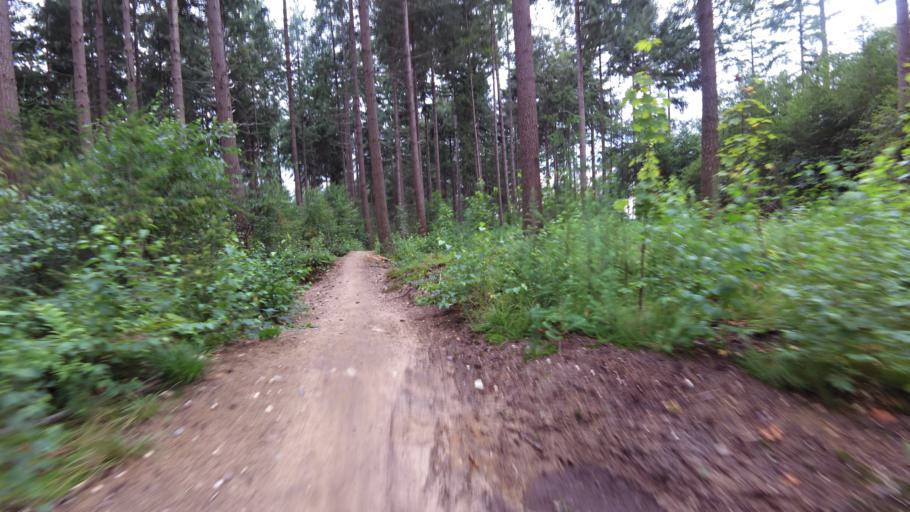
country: NL
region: Utrecht
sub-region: Gemeente Utrechtse Heuvelrug
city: Amerongen
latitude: 52.0022
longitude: 5.4866
